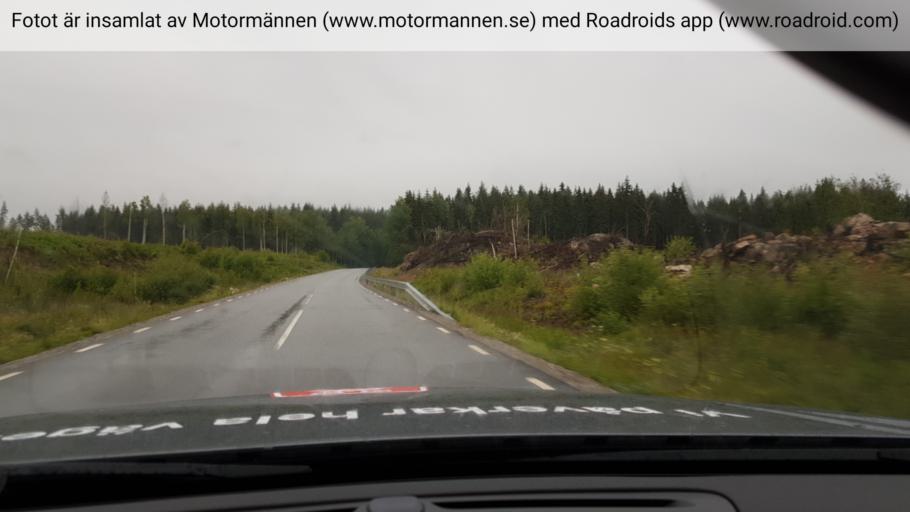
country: SE
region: Vaestmanland
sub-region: Norbergs Kommun
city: Norberg
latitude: 59.9938
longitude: 16.0687
